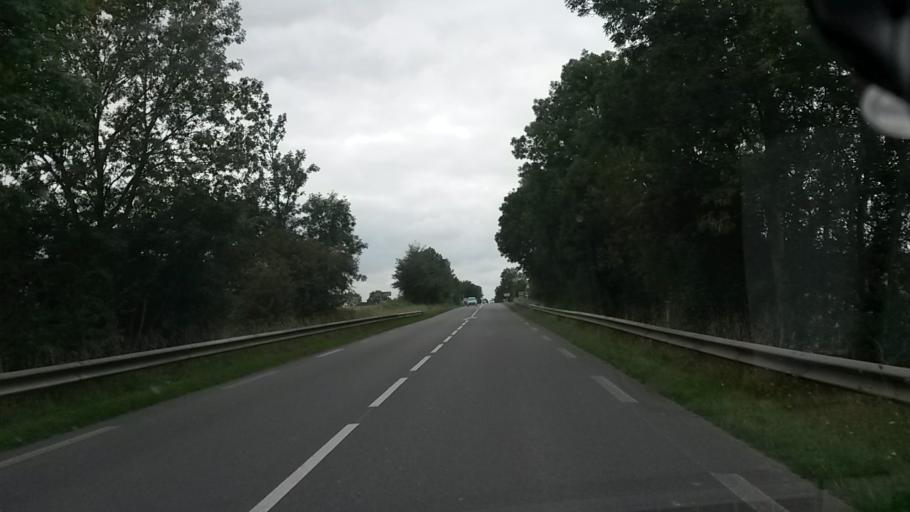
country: FR
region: Picardie
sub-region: Departement de la Somme
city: Corbie
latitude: 49.9748
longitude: 2.5562
